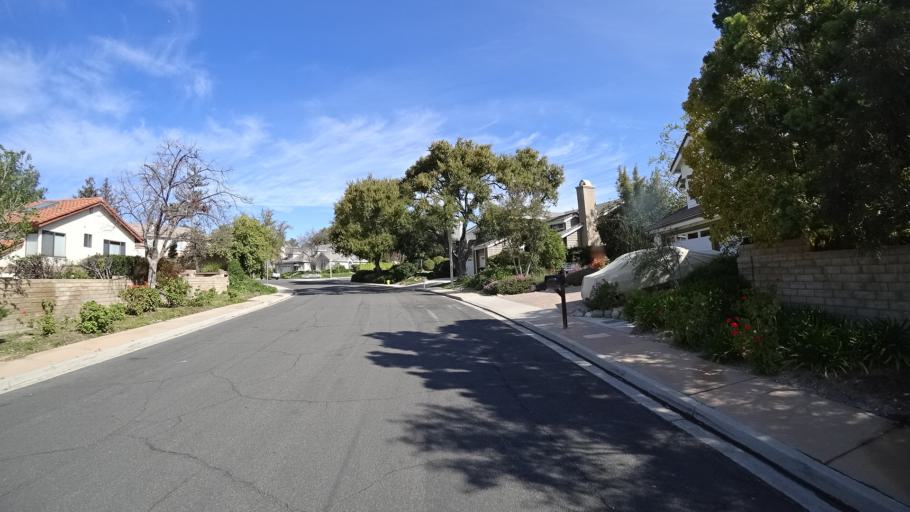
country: US
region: California
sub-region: Ventura County
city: Thousand Oaks
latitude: 34.2153
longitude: -118.8377
